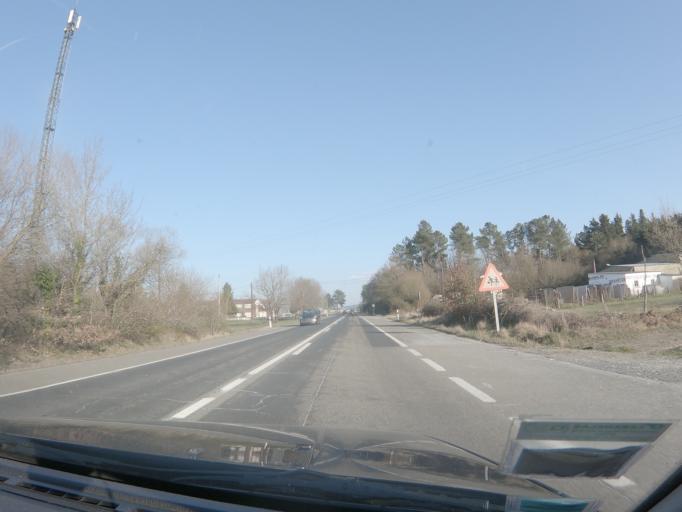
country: ES
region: Galicia
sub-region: Provincia de Lugo
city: Corgo
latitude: 42.9369
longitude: -7.4112
